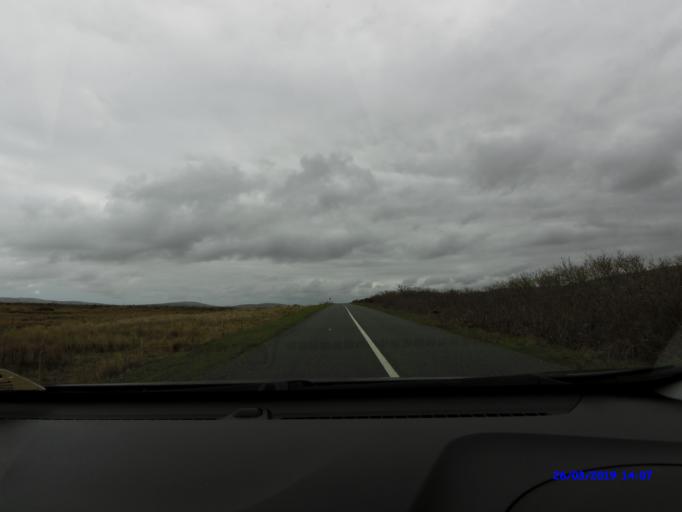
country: IE
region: Connaught
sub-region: Maigh Eo
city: Belmullet
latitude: 54.2081
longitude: -9.9119
